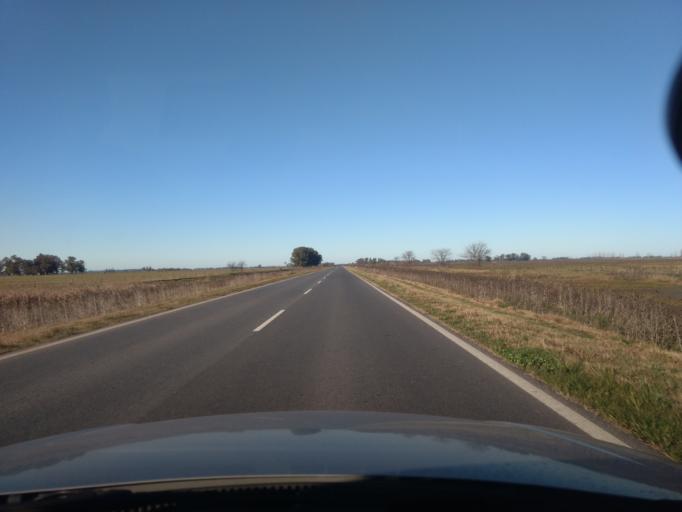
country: AR
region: Buenos Aires
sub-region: Partido de Navarro
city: Navarro
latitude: -34.8854
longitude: -59.2194
